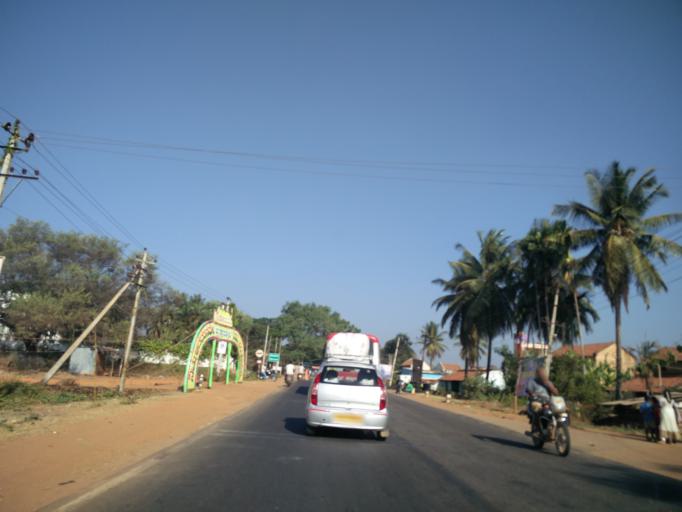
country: IN
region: Karnataka
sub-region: Tumkur
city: Gubbi
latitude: 13.3088
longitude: 76.9254
